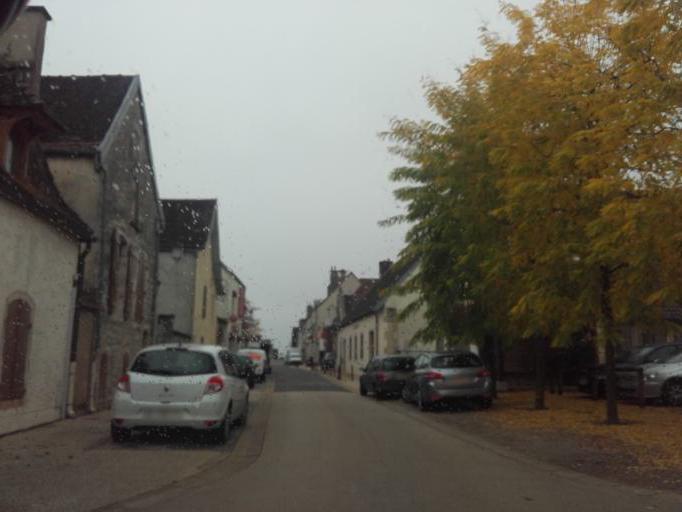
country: FR
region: Bourgogne
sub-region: Departement de la Cote-d'Or
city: Nuits-Saint-Georges
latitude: 47.1775
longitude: 4.9645
